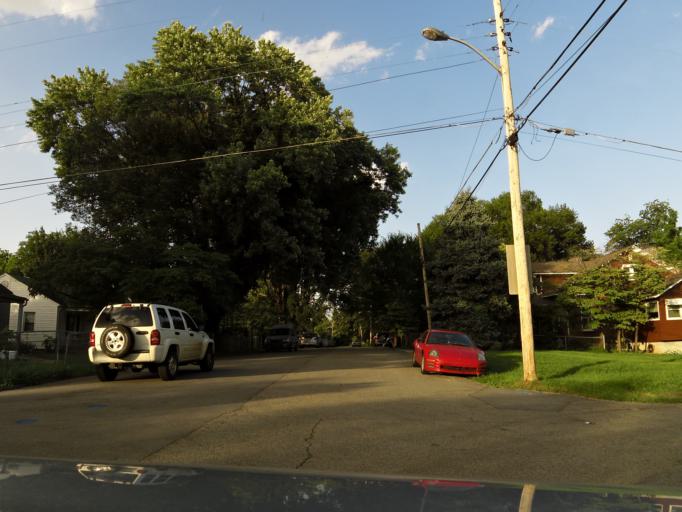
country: US
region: Tennessee
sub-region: Knox County
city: Knoxville
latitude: 35.9592
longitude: -83.9075
